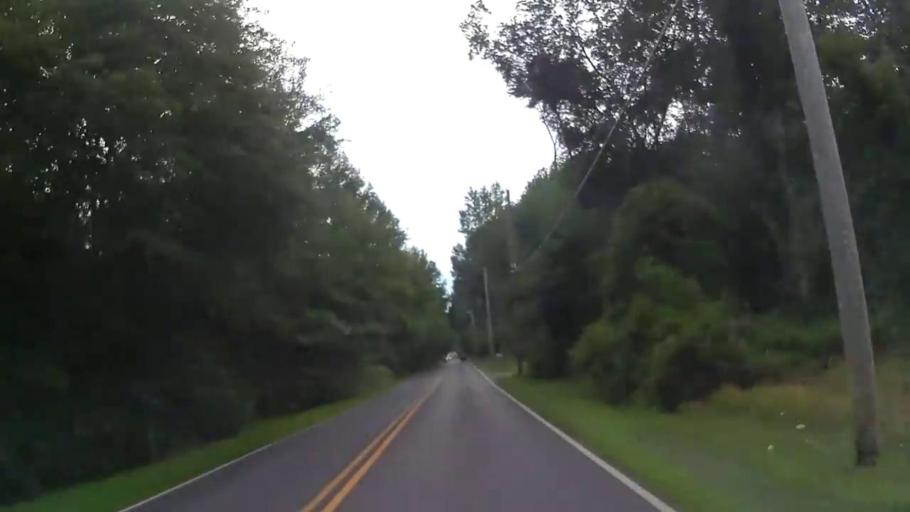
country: US
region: New Jersey
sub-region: Burlington County
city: Marlton
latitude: 39.8538
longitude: -74.9155
